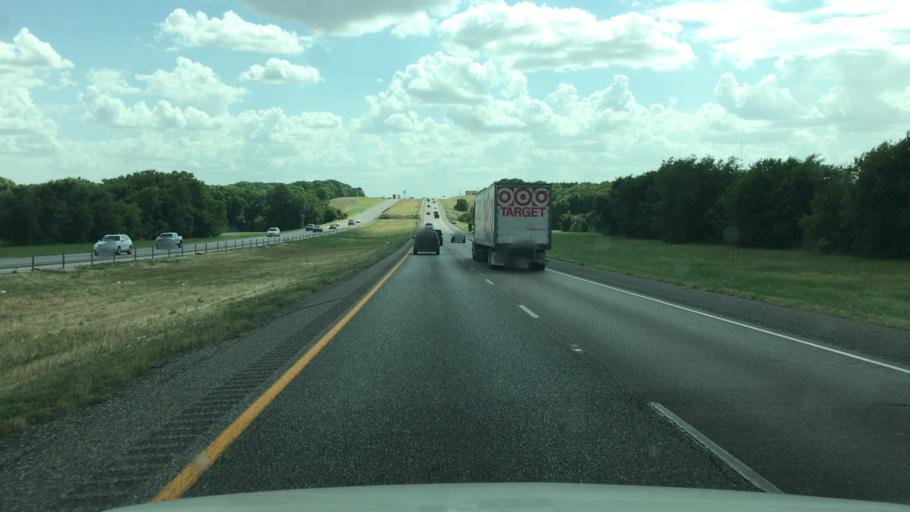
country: US
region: Texas
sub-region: Ellis County
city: Plum Grove
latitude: 32.0966
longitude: -97.0227
